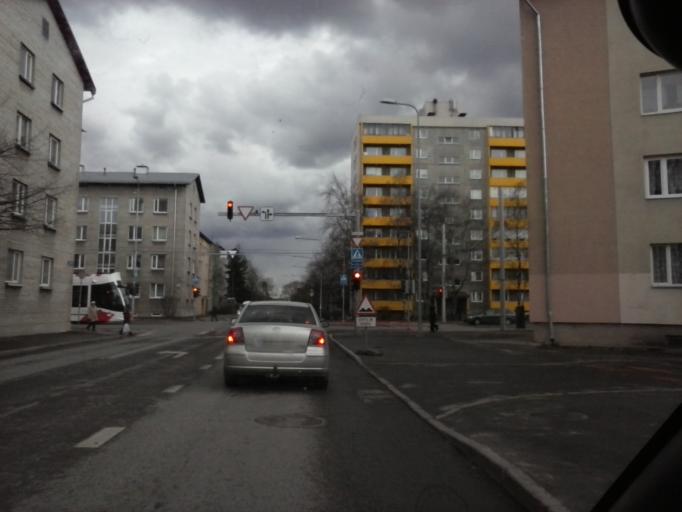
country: EE
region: Harju
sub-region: Tallinna linn
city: Tallinn
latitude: 59.4291
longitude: 24.7905
